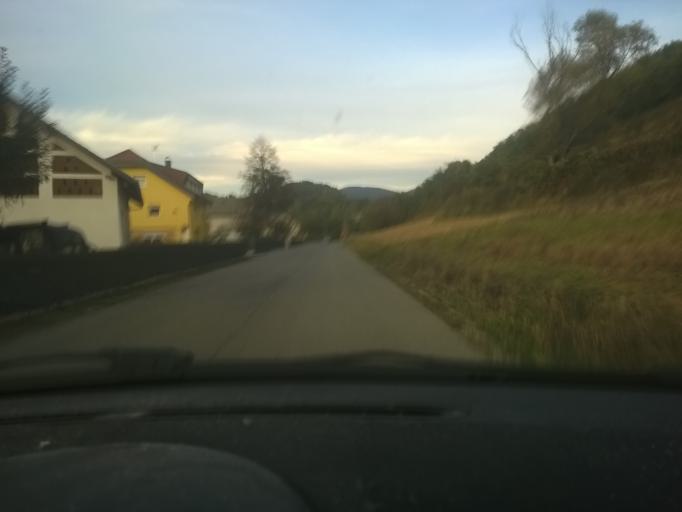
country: HR
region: Krapinsko-Zagorska
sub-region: Grad Krapina
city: Krapina
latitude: 46.1505
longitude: 15.8527
